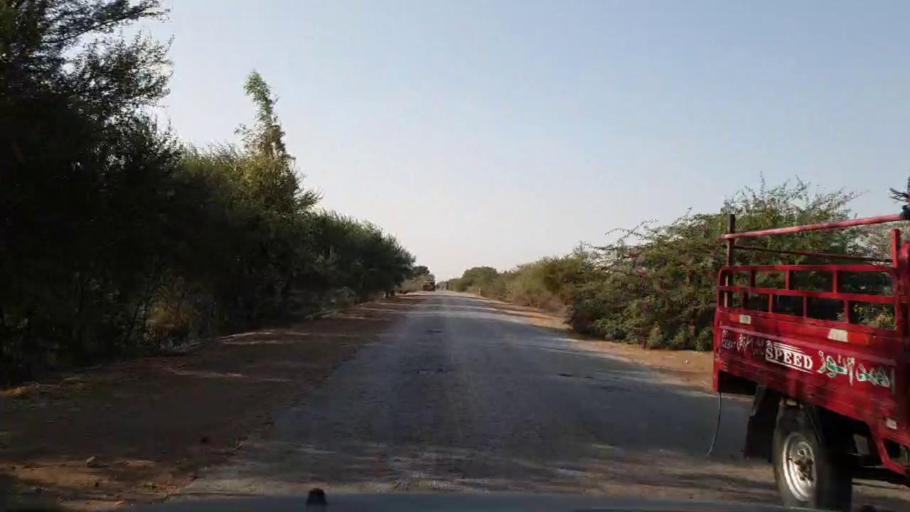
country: PK
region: Sindh
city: Tando Ghulam Ali
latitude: 25.1917
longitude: 68.8073
